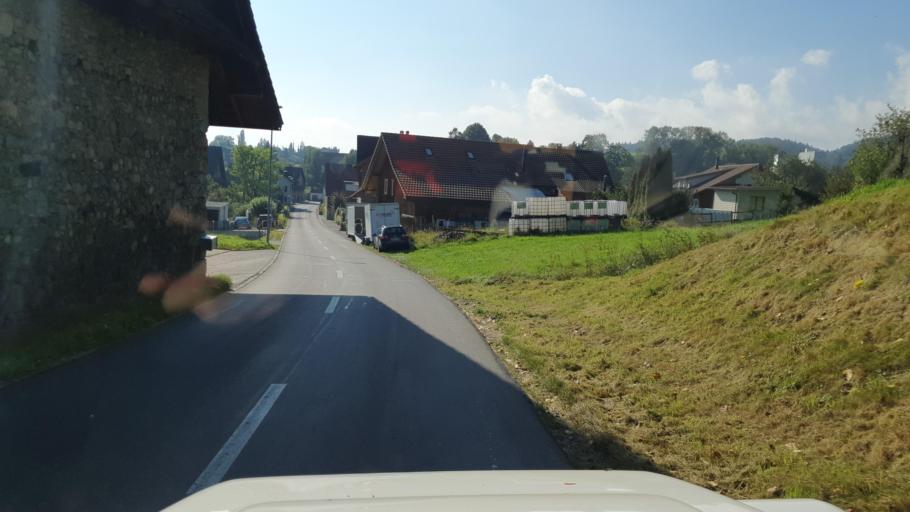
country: CH
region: Aargau
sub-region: Bezirk Muri
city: Buttwil
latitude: 47.3005
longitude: 8.3070
